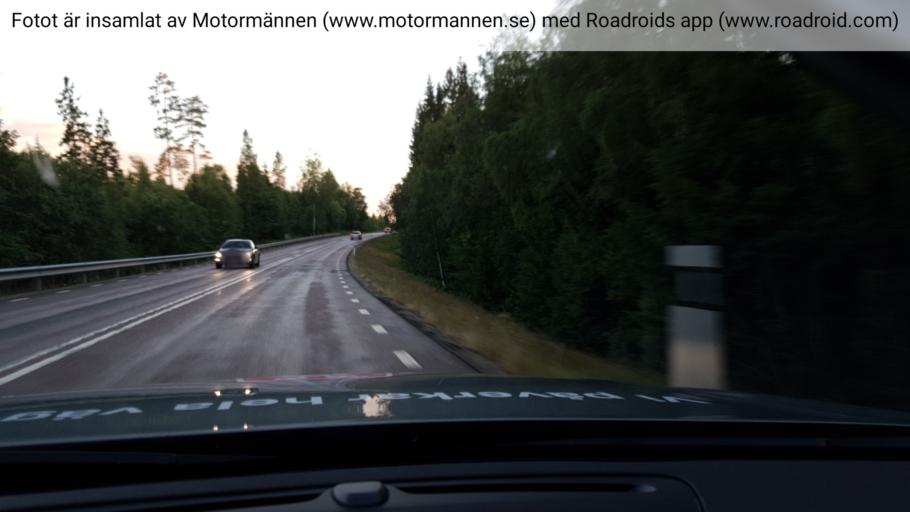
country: SE
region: Vaestmanland
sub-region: Skinnskattebergs Kommun
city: Skinnskatteberg
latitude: 59.9272
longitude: 15.7238
